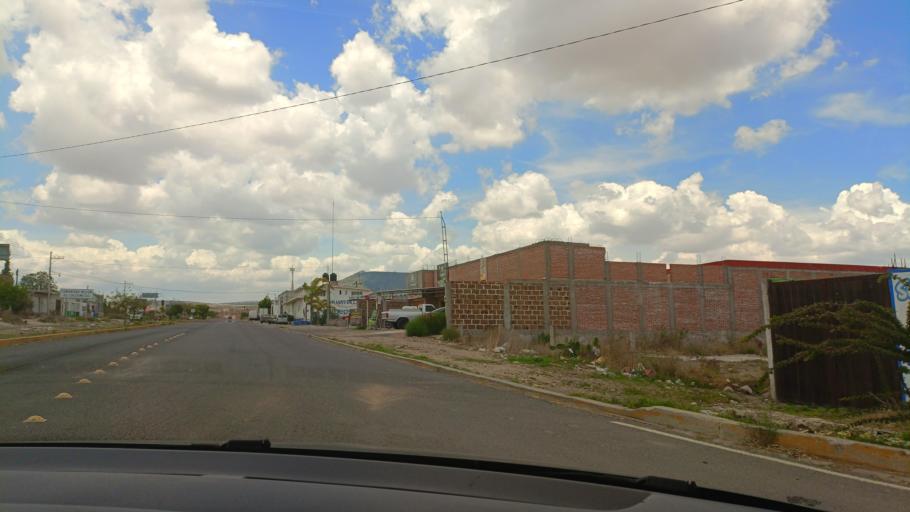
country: MX
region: Guanajuato
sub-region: San Luis de la Paz
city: San Luis de la Paz
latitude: 21.2952
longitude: -100.4898
